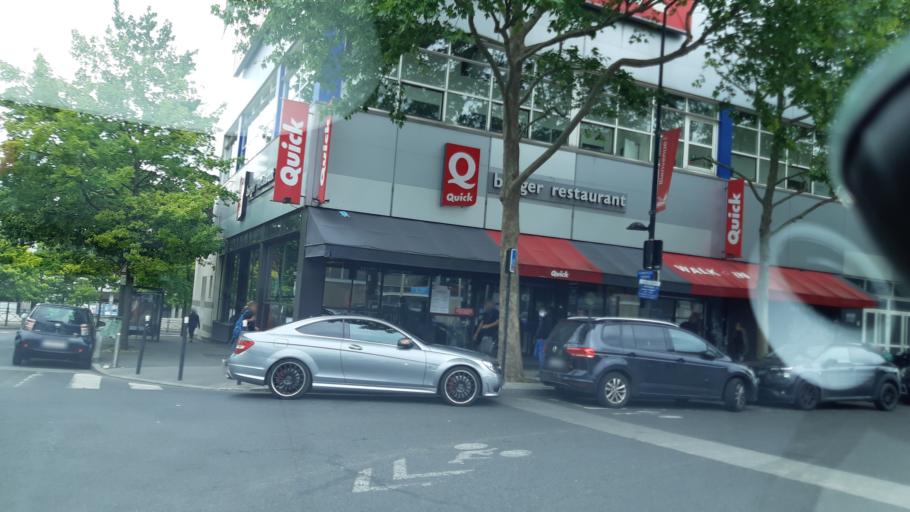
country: FR
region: Ile-de-France
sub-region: Departement de Seine-Saint-Denis
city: Saint-Denis
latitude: 48.9261
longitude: 2.3623
